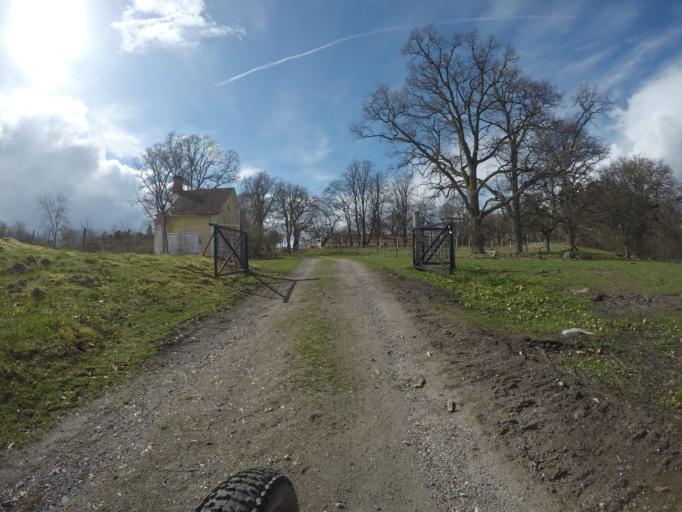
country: SE
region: Vaestmanland
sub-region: Kungsors Kommun
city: Kungsoer
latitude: 59.2723
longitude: 16.1244
